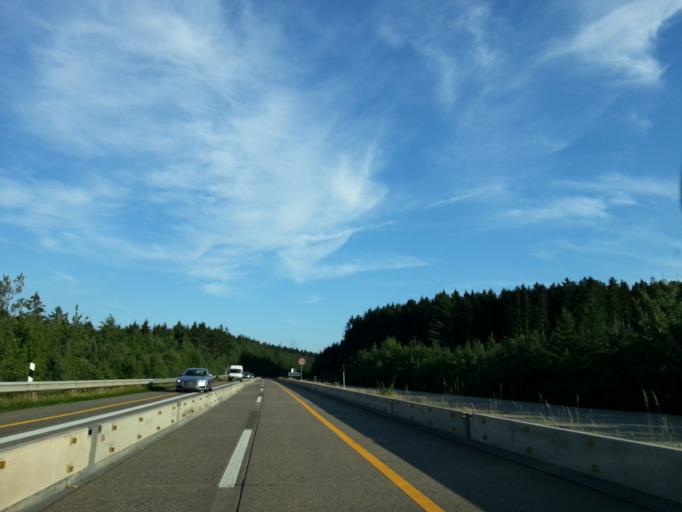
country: DE
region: Rheinland-Pfalz
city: Hinzert-Polert
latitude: 49.7213
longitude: 6.8905
